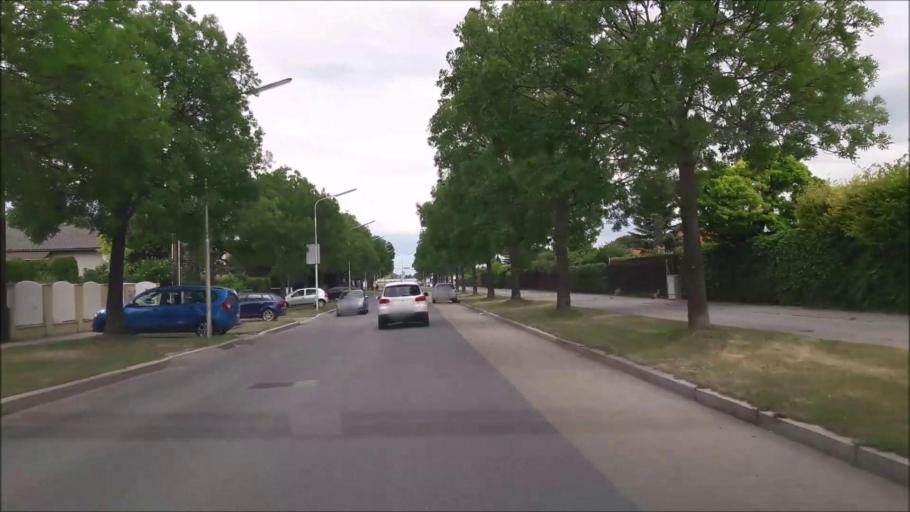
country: AT
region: Lower Austria
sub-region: Politischer Bezirk Ganserndorf
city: Gross-Enzersdorf
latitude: 48.2255
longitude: 16.4839
